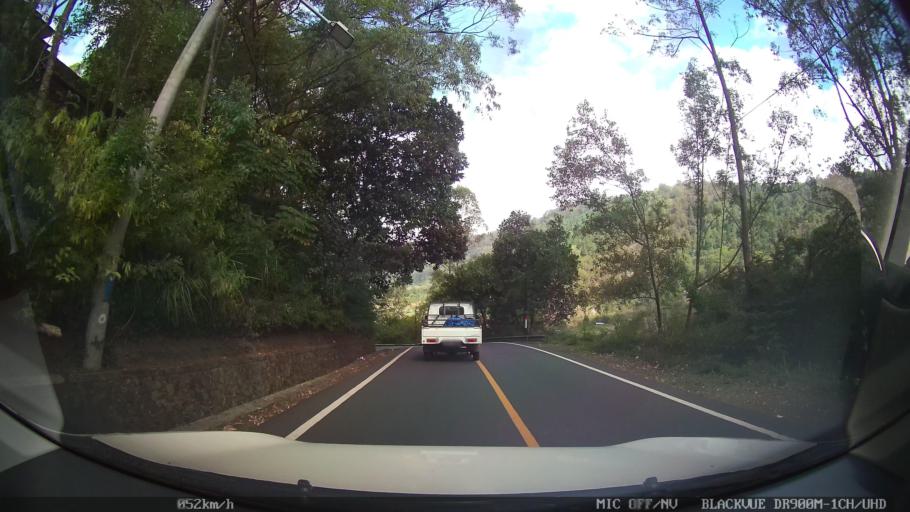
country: ID
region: Bali
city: Banjar Kedisan
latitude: -8.2778
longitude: 115.3742
